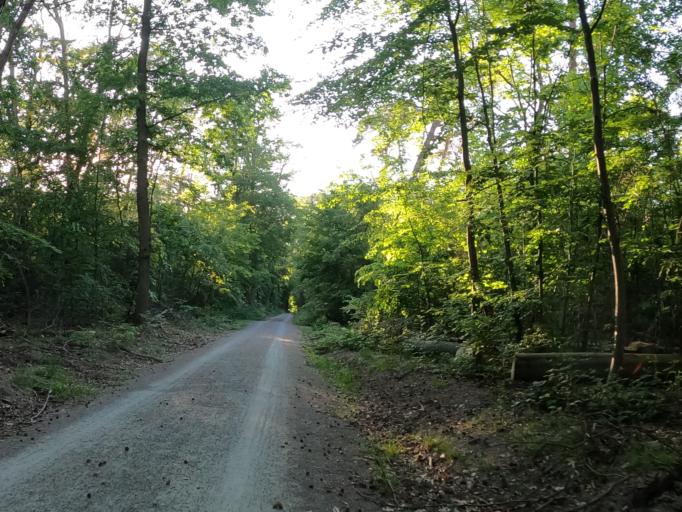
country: DE
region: Hesse
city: Kelsterbach
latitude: 50.0642
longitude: 8.5756
